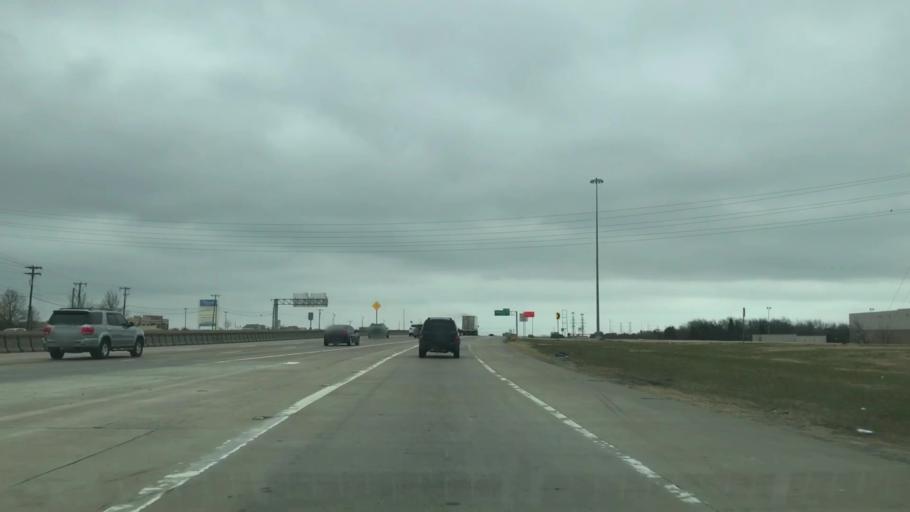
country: US
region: Texas
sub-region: Dallas County
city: Mesquite
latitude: 32.8262
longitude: -96.6240
